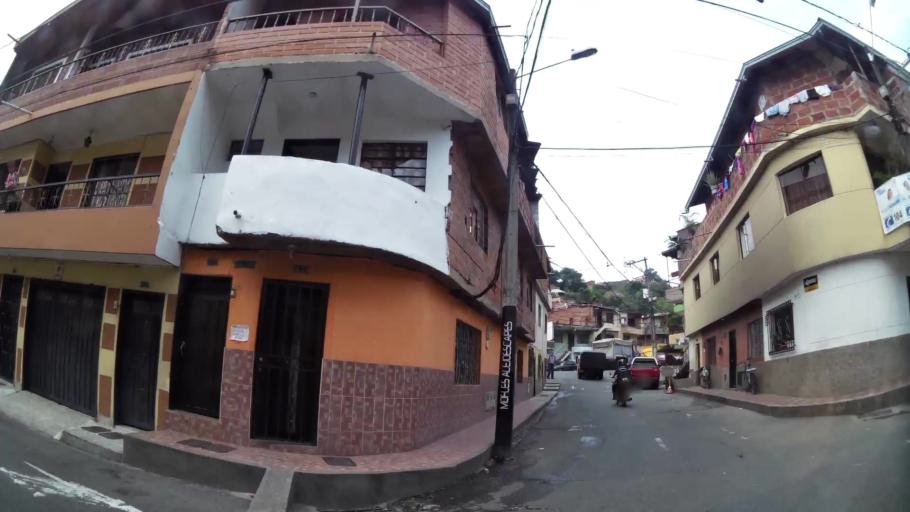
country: CO
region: Antioquia
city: Itagui
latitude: 6.1851
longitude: -75.6025
